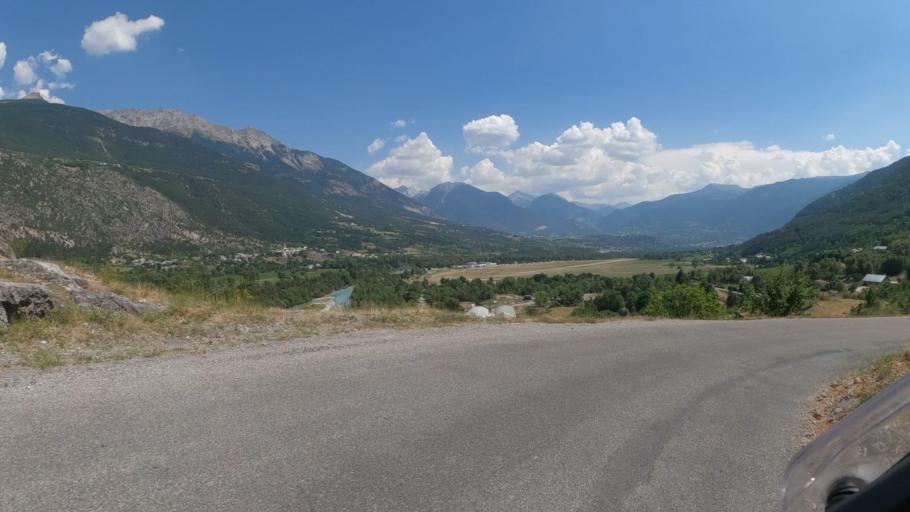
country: FR
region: Provence-Alpes-Cote d'Azur
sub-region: Departement des Hautes-Alpes
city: Guillestre
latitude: 44.7097
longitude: 6.5893
